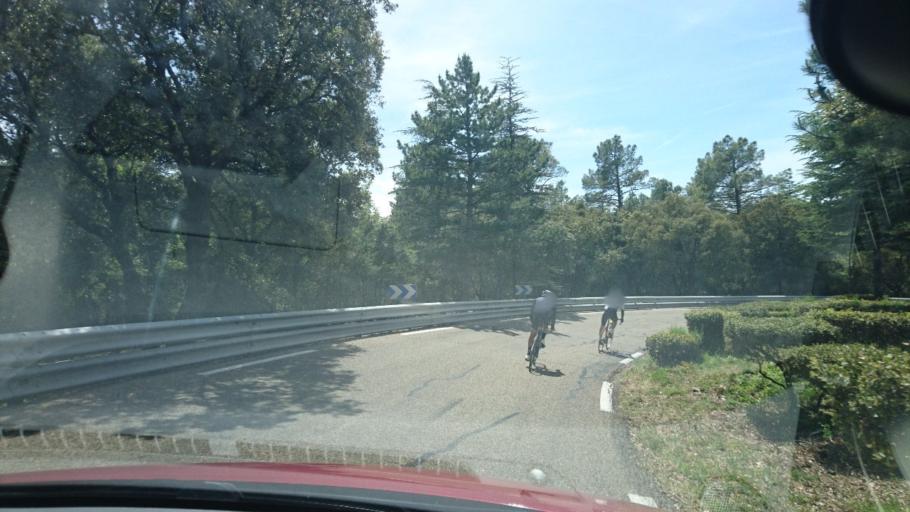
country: FR
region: Provence-Alpes-Cote d'Azur
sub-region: Departement du Vaucluse
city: Villes-sur-Auzon
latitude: 44.1154
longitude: 5.2442
